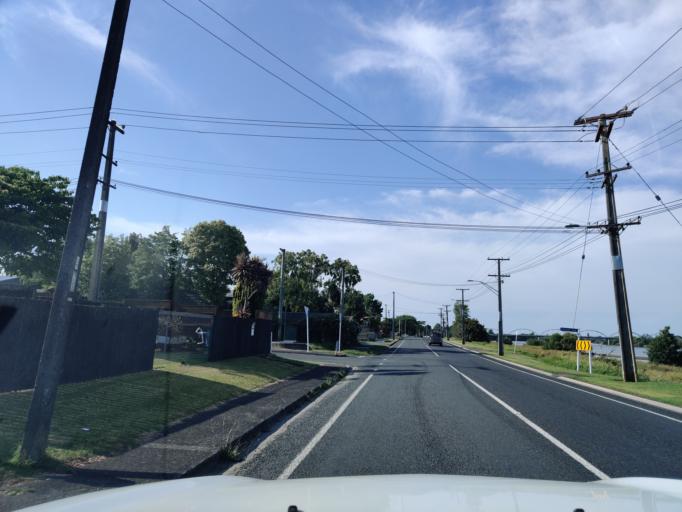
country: NZ
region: Waikato
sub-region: Waikato District
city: Ngaruawahia
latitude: -37.5730
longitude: 175.1525
